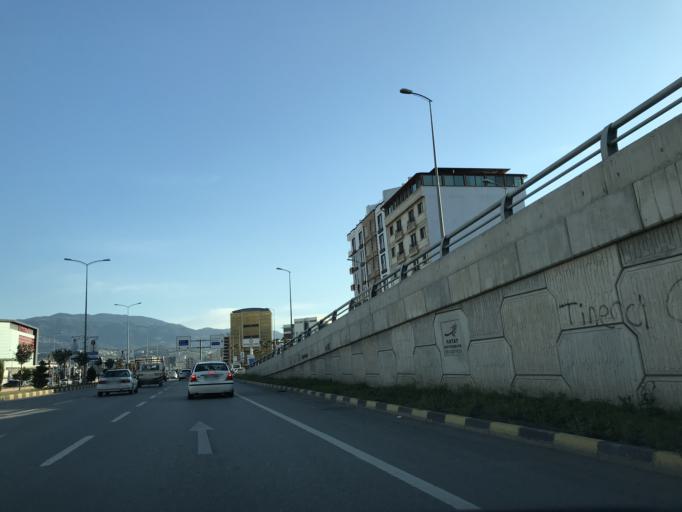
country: TR
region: Hatay
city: Iskenderun
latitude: 36.5775
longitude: 36.1618
